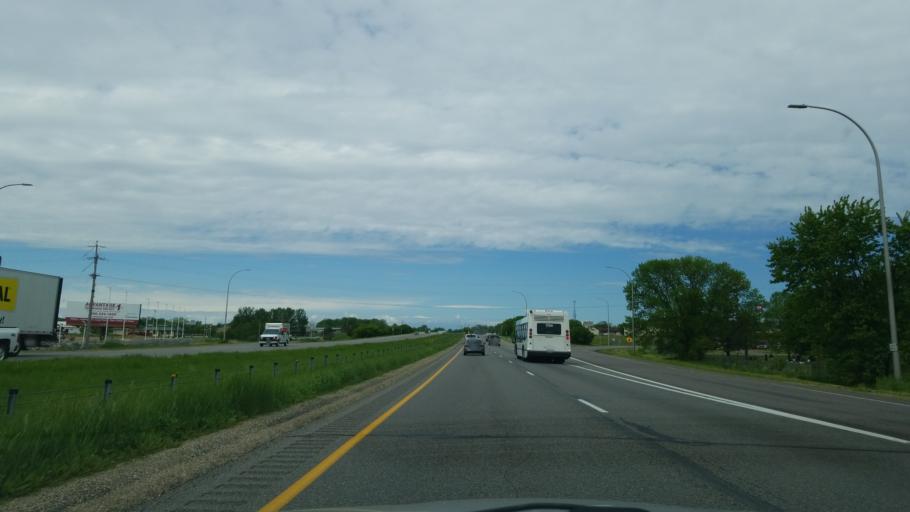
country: US
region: Minnesota
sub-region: Stearns County
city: Albany
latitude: 45.6257
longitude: -94.5714
